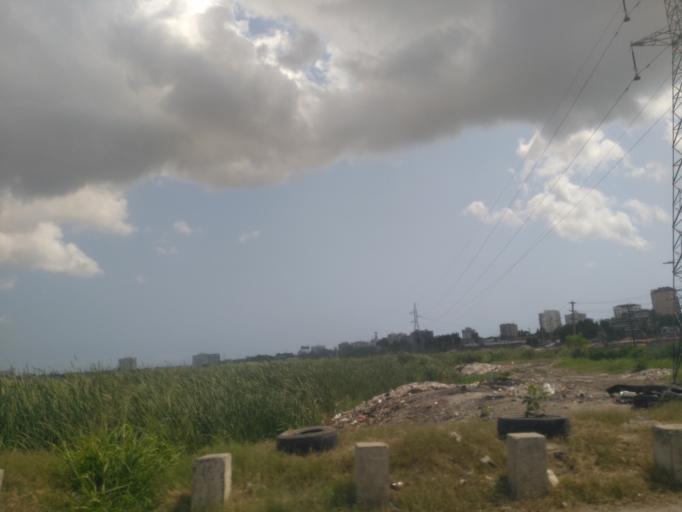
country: TZ
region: Dar es Salaam
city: Dar es Salaam
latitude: -6.8163
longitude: 39.2683
